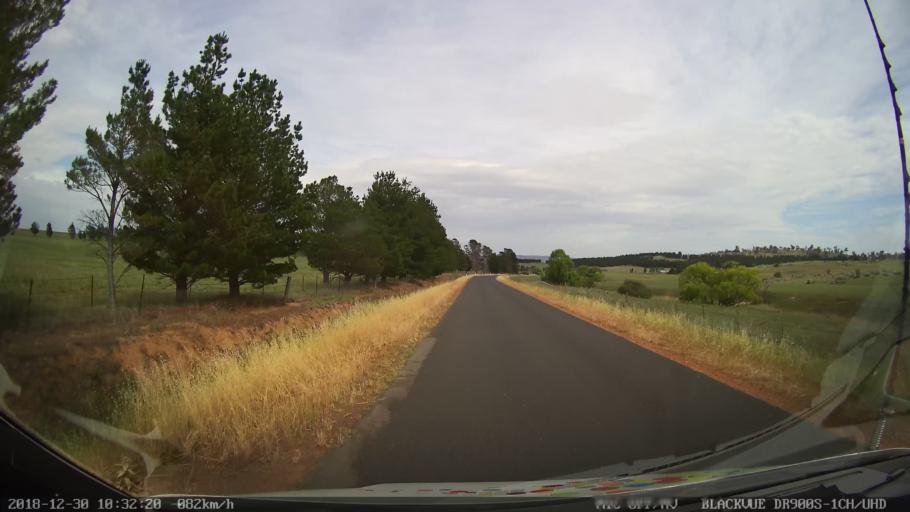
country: AU
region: New South Wales
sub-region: Snowy River
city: Berridale
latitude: -36.5013
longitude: 148.8676
